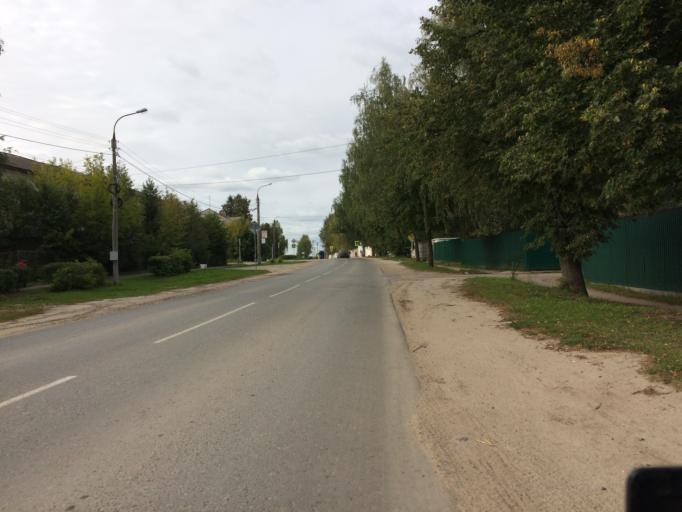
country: RU
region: Mariy-El
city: Yoshkar-Ola
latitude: 56.6525
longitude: 47.9789
